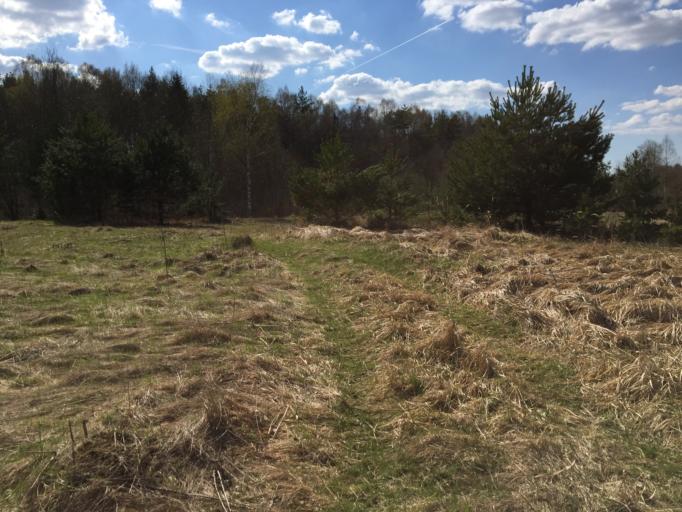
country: LV
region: Krimulda
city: Ragana
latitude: 57.3416
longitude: 24.7003
